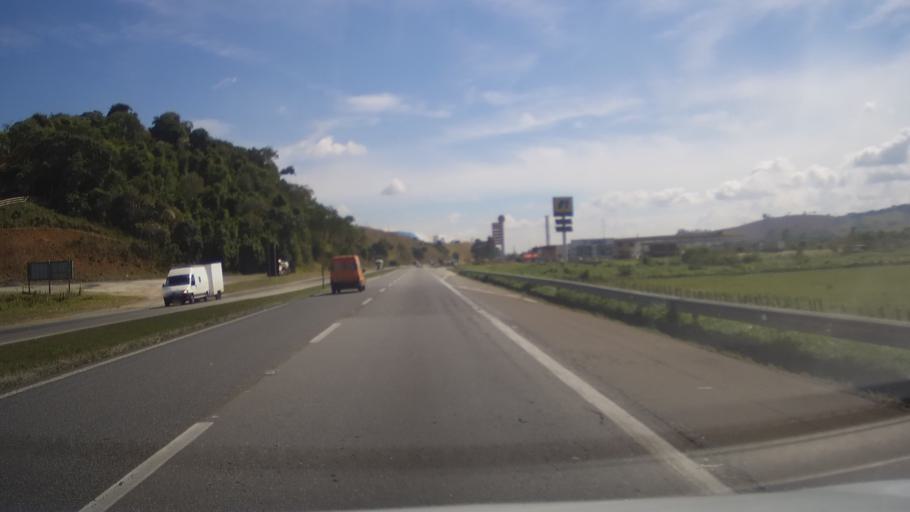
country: BR
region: Minas Gerais
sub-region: Cambui
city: Cambui
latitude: -22.5302
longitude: -46.0273
